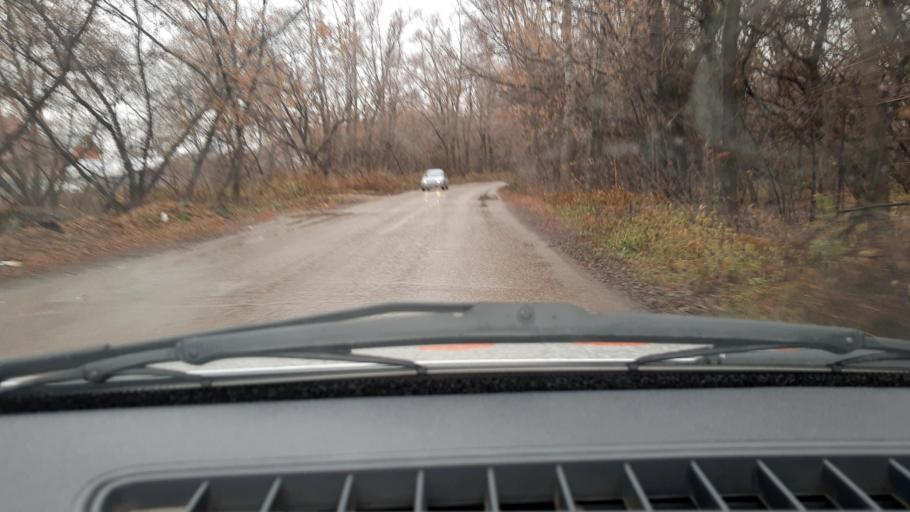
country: RU
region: Bashkortostan
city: Ufa
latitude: 54.8029
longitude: 56.1515
